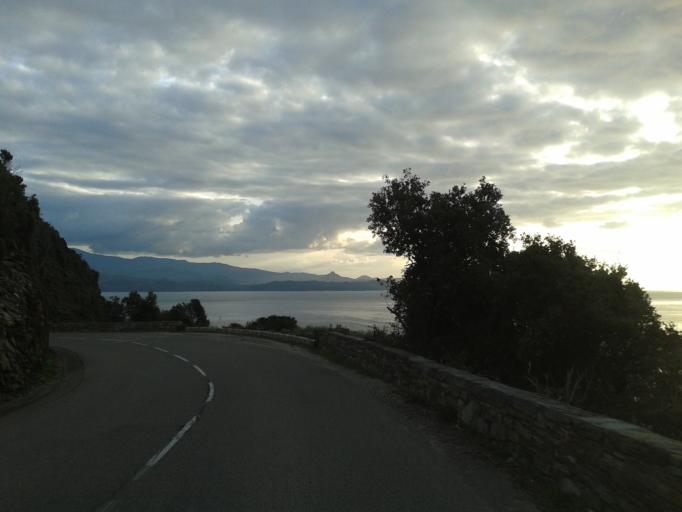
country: FR
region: Corsica
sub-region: Departement de la Haute-Corse
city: Santa-Maria-di-Lota
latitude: 42.7681
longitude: 9.3412
